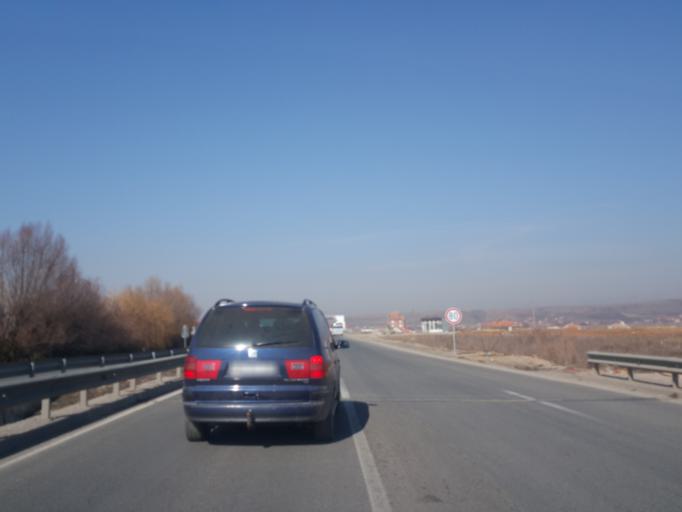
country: XK
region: Pristina
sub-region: Komuna e Obiliqit
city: Obiliq
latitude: 42.7269
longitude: 21.0786
